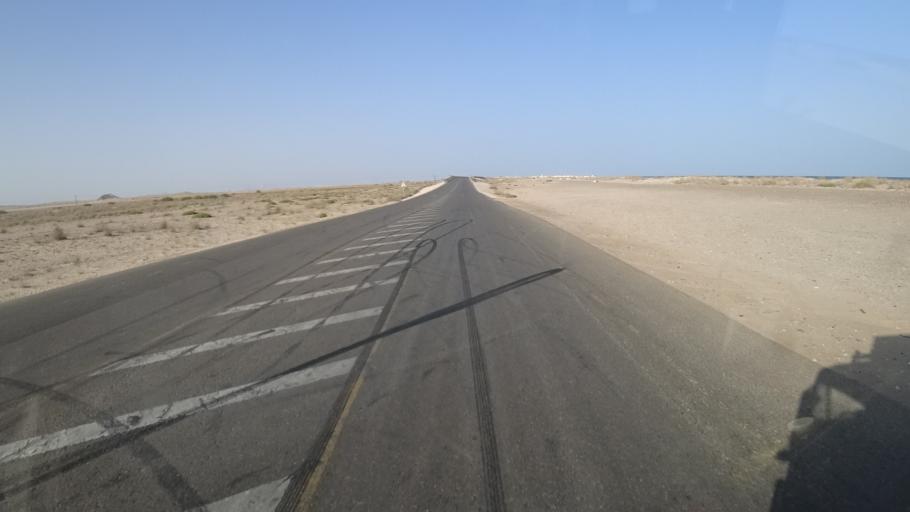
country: OM
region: Ash Sharqiyah
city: Sur
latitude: 22.1511
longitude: 59.7383
